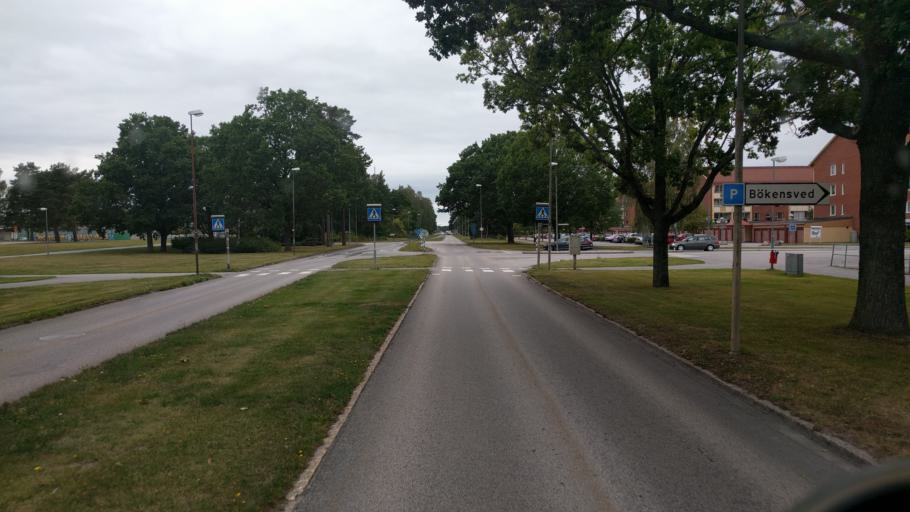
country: SE
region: Kalmar
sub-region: Vasterviks Kommun
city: Vaestervik
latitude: 57.7479
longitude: 16.6402
